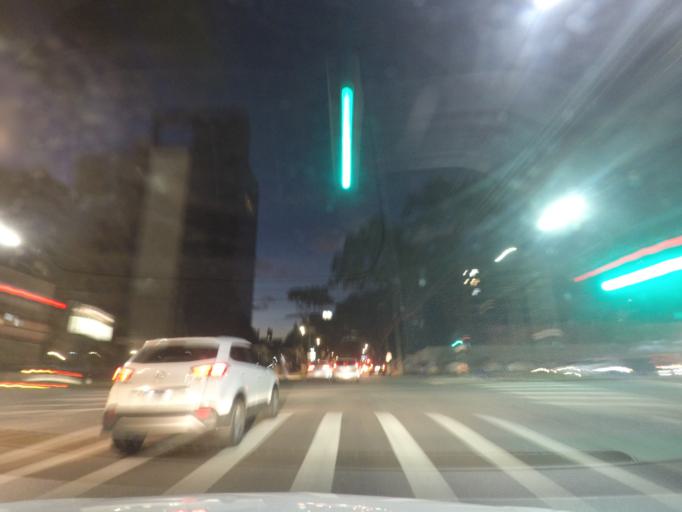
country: BR
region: Parana
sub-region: Curitiba
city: Curitiba
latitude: -25.4422
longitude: -49.2815
